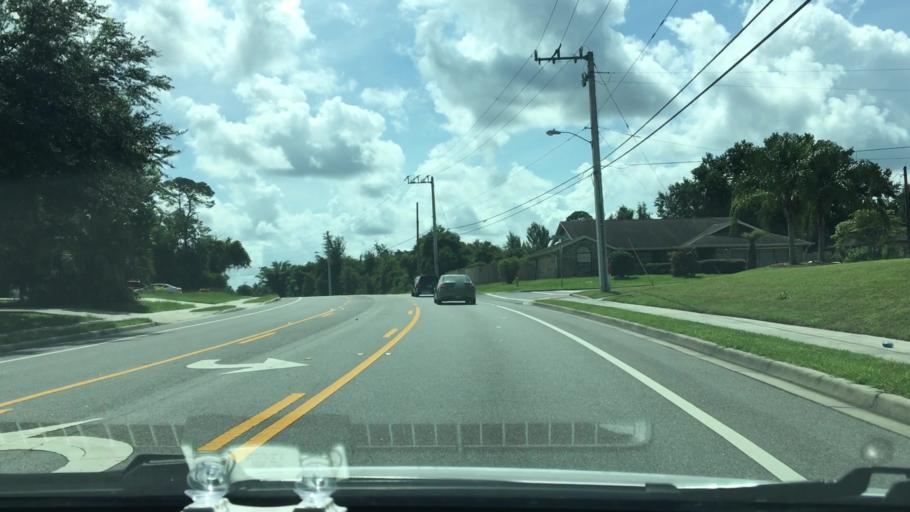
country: US
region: Florida
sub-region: Volusia County
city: Deltona
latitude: 28.8895
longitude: -81.2151
